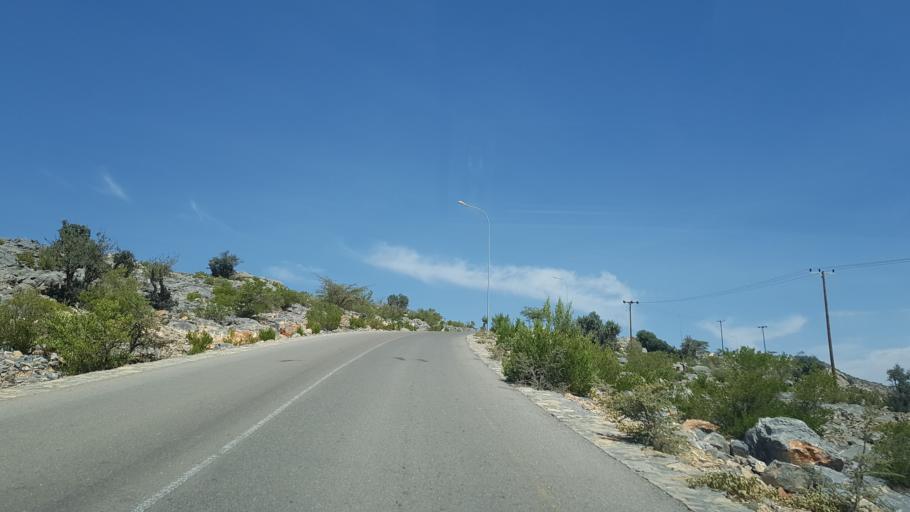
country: OM
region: Al Batinah
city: Bayt al `Awabi
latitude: 23.1369
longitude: 57.5547
